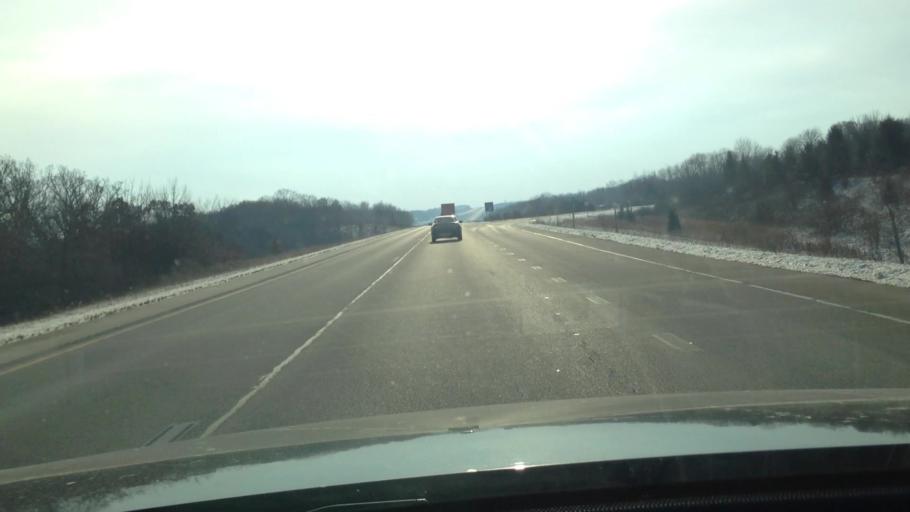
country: US
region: Wisconsin
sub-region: Walworth County
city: East Troy
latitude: 42.7373
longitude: -88.4566
